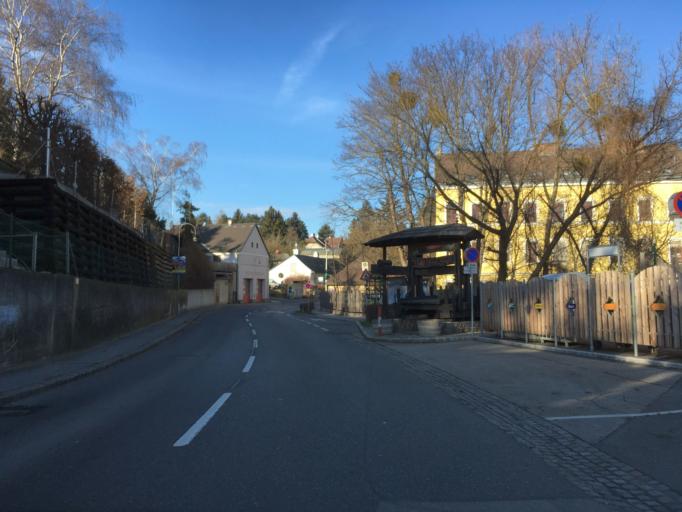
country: AT
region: Lower Austria
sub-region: Politischer Bezirk Wien-Umgebung
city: Klosterneuburg
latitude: 48.3255
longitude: 16.3040
